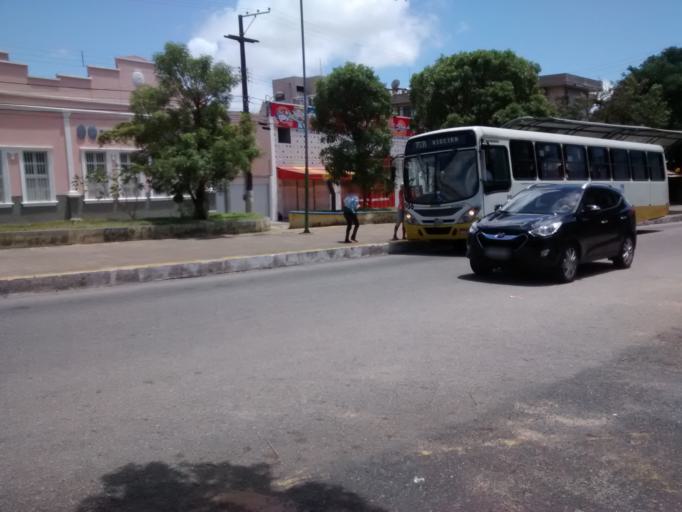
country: BR
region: Rio Grande do Norte
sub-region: Natal
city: Natal
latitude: -5.7845
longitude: -35.2089
